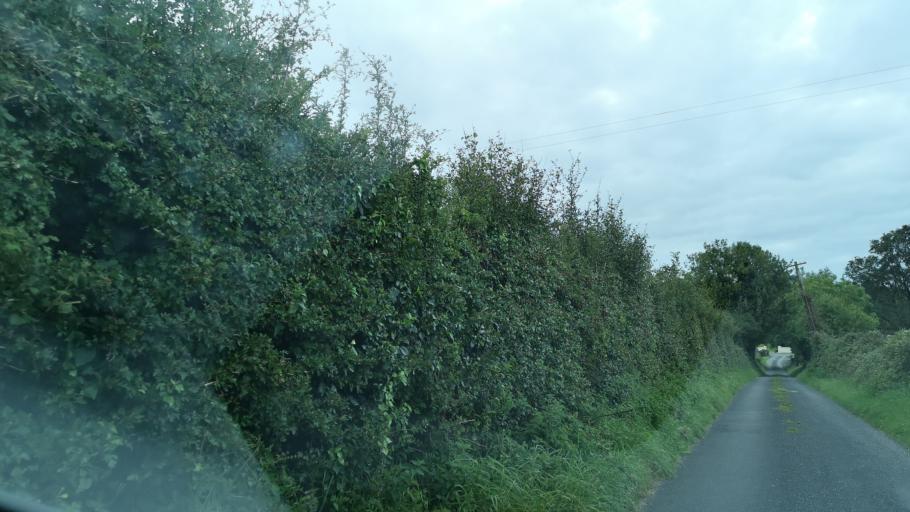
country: IE
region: Connaught
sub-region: County Galway
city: Loughrea
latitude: 53.1612
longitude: -8.4702
